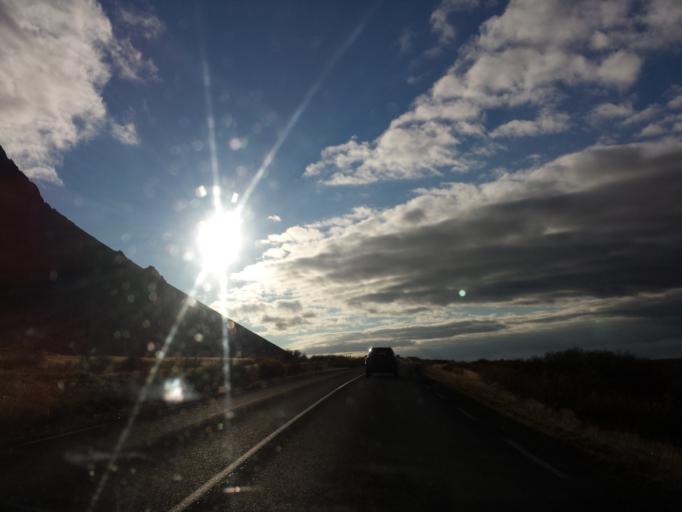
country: IS
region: West
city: Borgarnes
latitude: 64.5139
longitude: -21.8944
